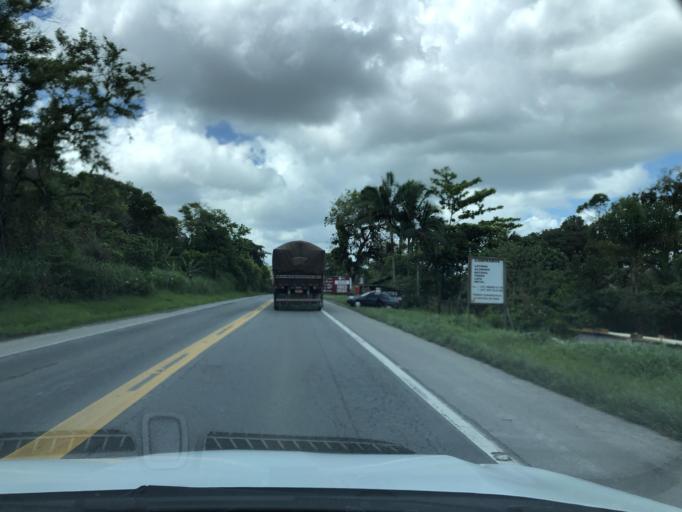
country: BR
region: Santa Catarina
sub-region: Sao Francisco Do Sul
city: Sao Francisco do Sul
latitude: -26.3557
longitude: -48.6601
